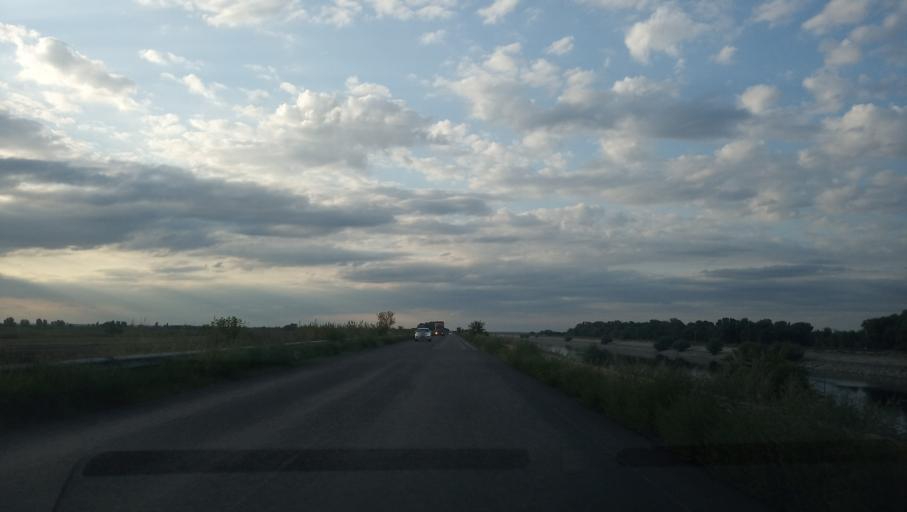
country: RO
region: Calarasi
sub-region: Municipiul Calarasi
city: Calarasi
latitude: 44.1770
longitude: 27.3071
